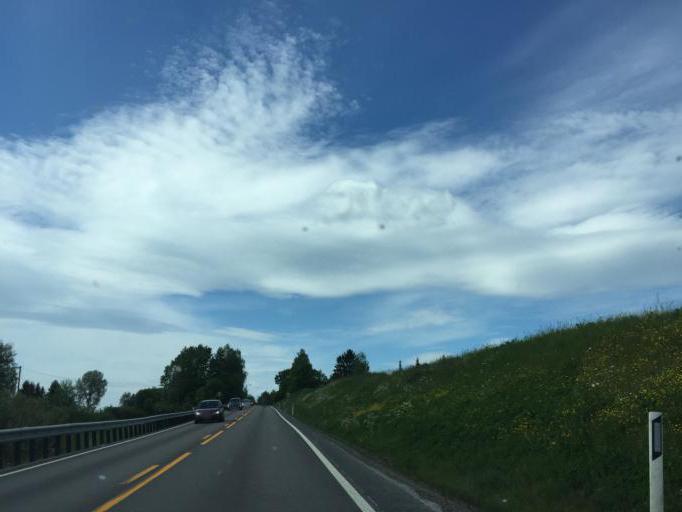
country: NO
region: Akershus
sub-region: Nes
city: Arnes
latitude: 60.1688
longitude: 11.4791
